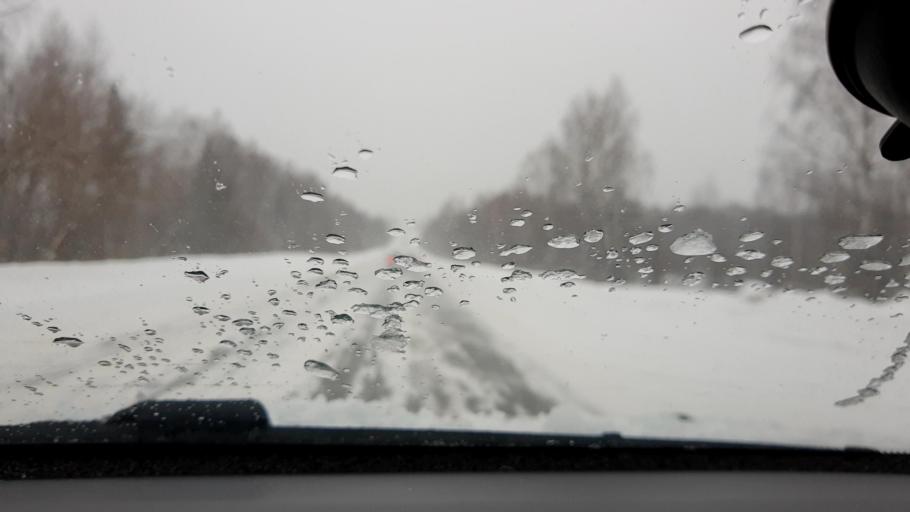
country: RU
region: Nizjnij Novgorod
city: Chkalovsk
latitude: 56.6287
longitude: 43.2152
